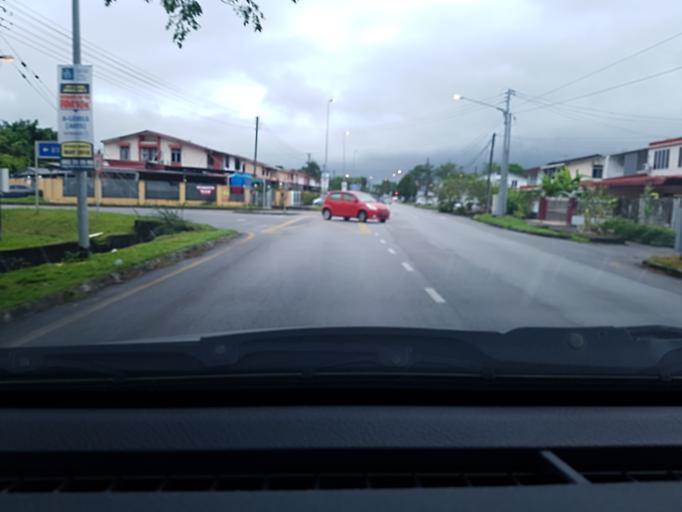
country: MY
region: Sarawak
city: Kuching
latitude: 1.5243
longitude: 110.3720
